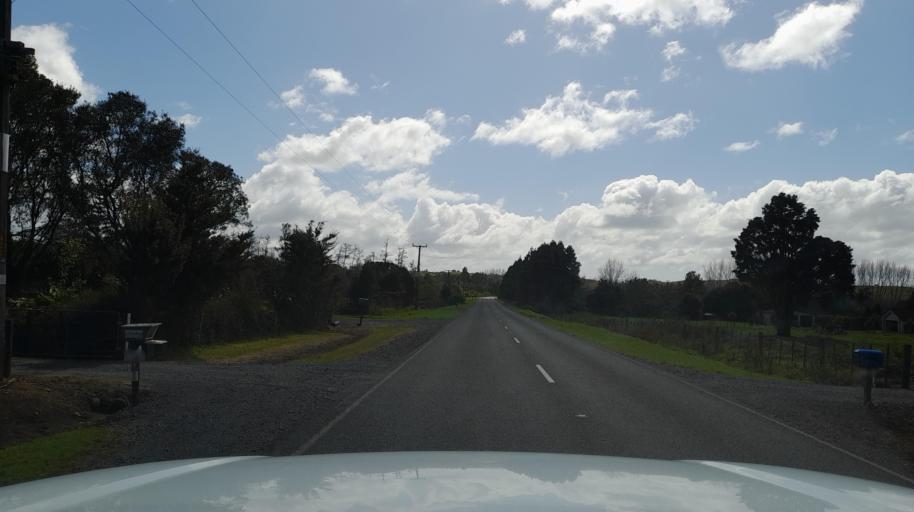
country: NZ
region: Northland
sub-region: Far North District
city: Kerikeri
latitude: -35.2356
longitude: 173.8782
